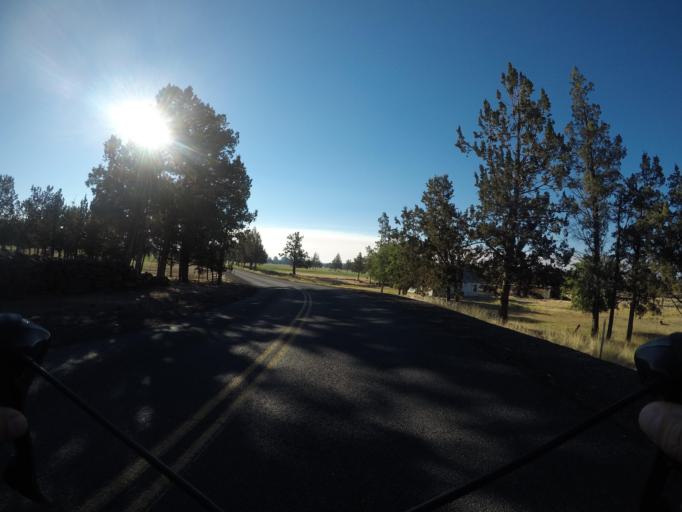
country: US
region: Oregon
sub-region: Deschutes County
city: Redmond
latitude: 44.2659
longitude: -121.2481
